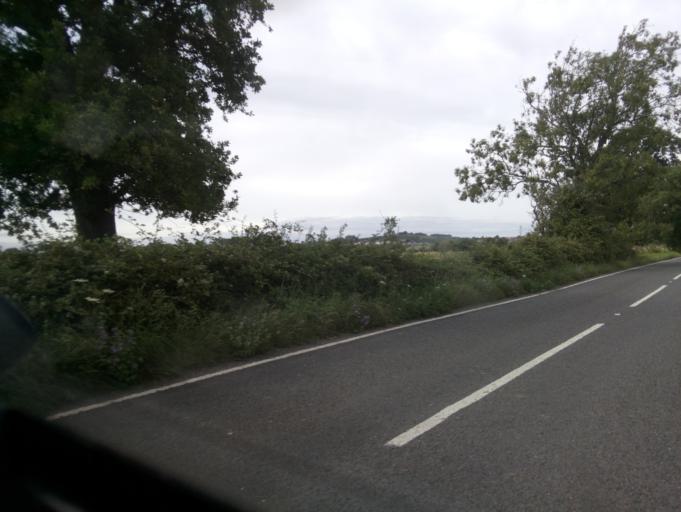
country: GB
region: England
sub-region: Somerset
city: Glastonbury
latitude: 51.1264
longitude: -2.7120
